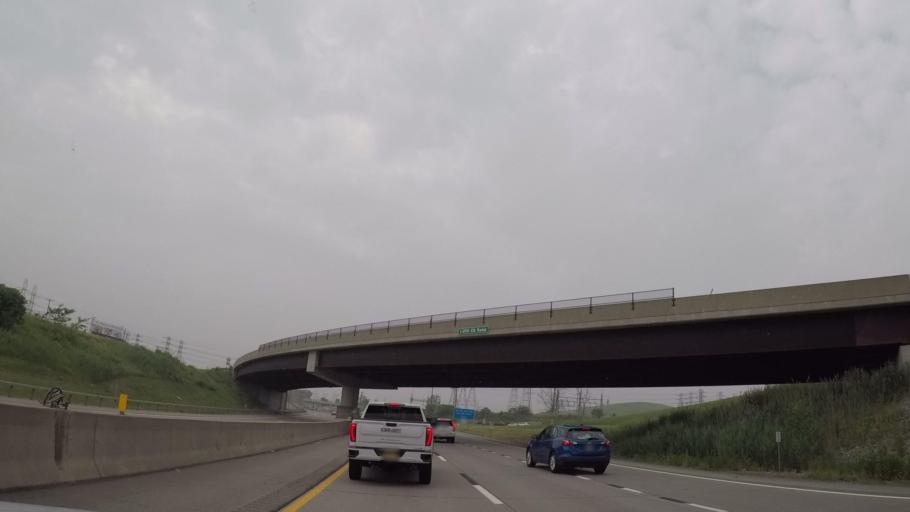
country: US
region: New York
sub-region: Erie County
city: Tonawanda
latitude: 42.9868
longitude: -78.9145
